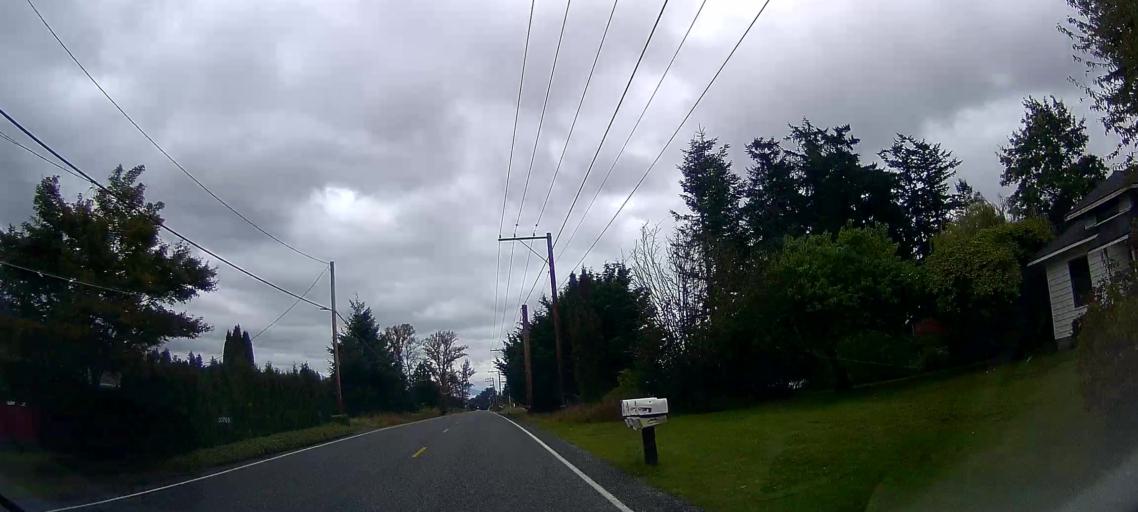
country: US
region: Washington
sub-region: Skagit County
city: Sedro-Woolley
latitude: 48.5270
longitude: -122.0775
